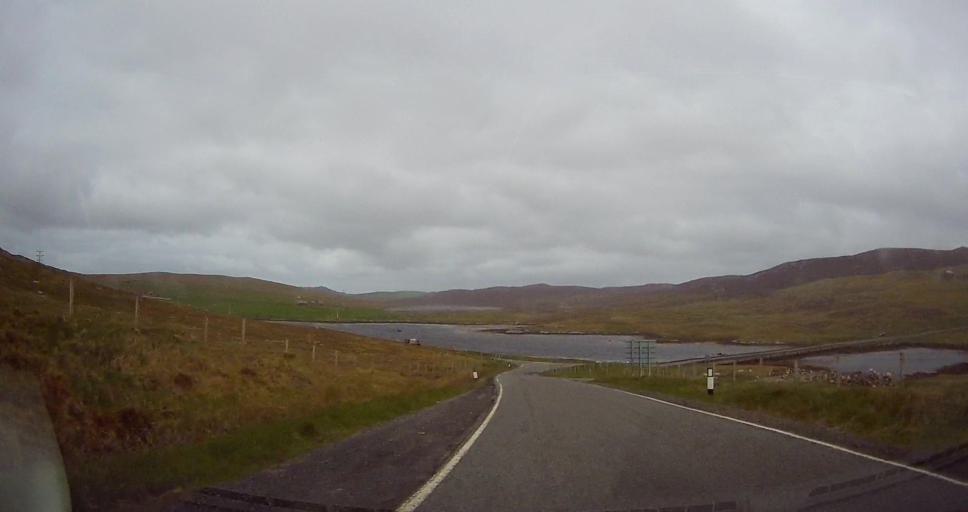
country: GB
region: Scotland
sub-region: Shetland Islands
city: Sandwick
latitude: 60.2431
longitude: -1.5326
